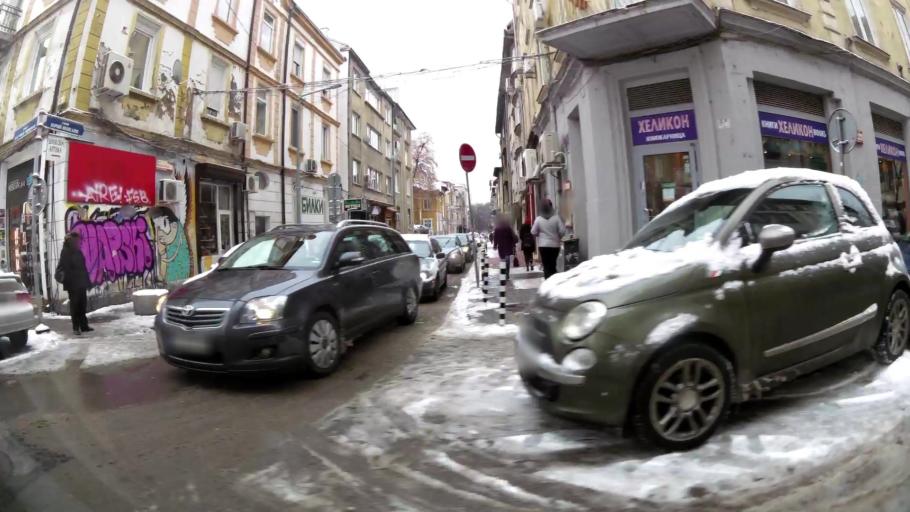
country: BG
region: Sofia-Capital
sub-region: Stolichna Obshtina
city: Sofia
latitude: 42.6906
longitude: 23.3288
